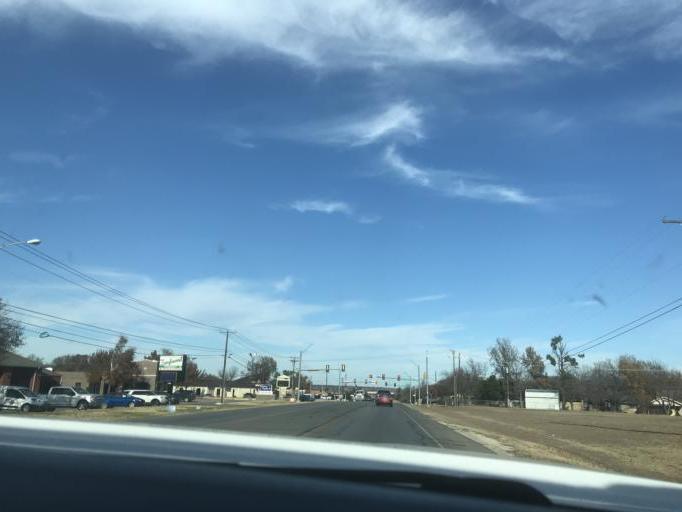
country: US
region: Texas
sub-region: Erath County
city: Stephenville
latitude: 32.2191
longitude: -98.2381
